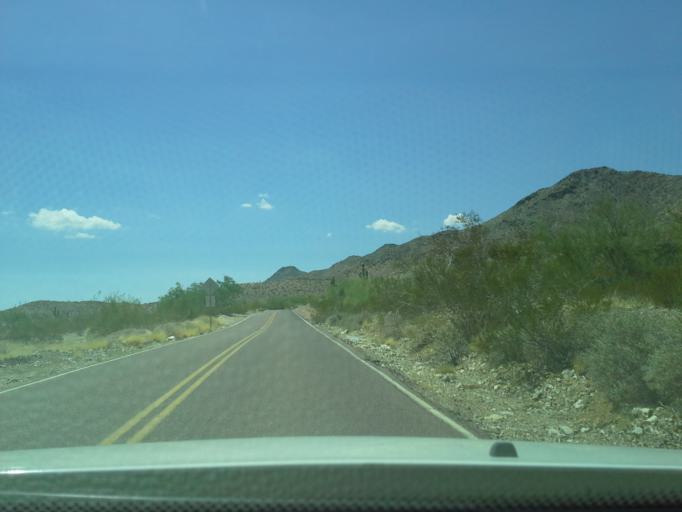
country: US
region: Arizona
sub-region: Maricopa County
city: Laveen
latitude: 33.3394
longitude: -112.0908
